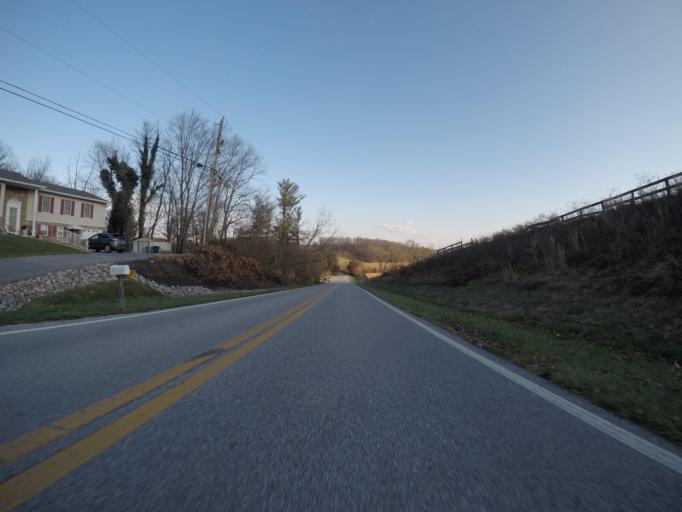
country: US
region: Maryland
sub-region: Carroll County
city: Hampstead
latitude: 39.5729
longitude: -76.9047
